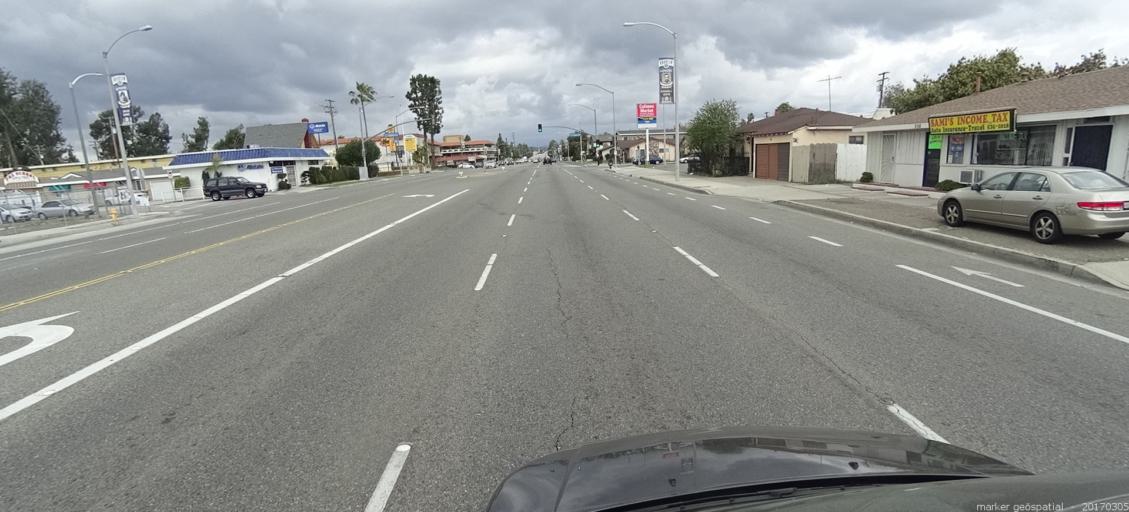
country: US
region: California
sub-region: Orange County
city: Anaheim
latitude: 33.8354
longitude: -117.9589
